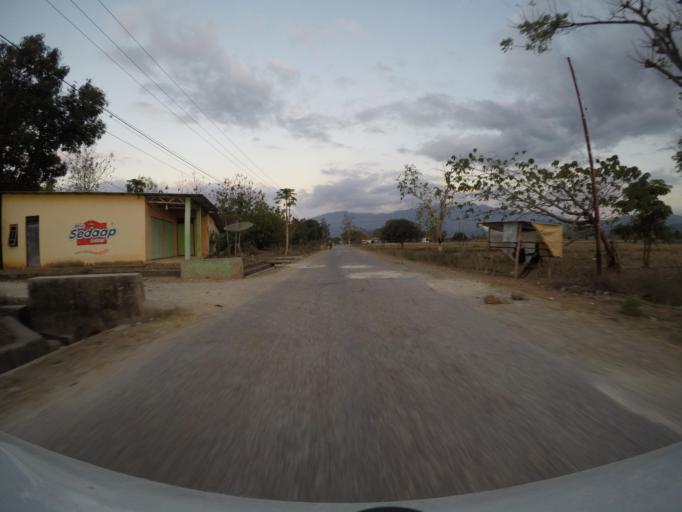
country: TL
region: Bobonaro
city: Maliana
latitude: -8.9754
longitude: 125.1408
